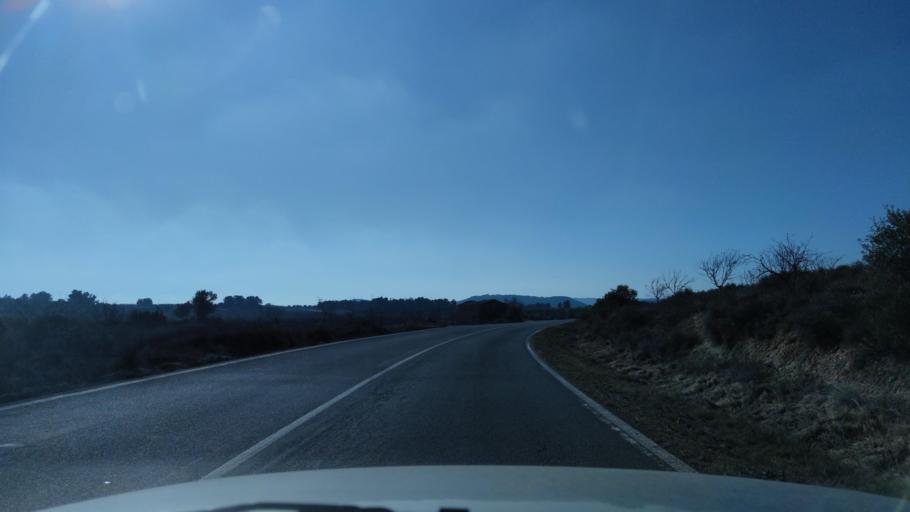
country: ES
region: Catalonia
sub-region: Provincia de Lleida
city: Maials
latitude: 41.3559
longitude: 0.4724
